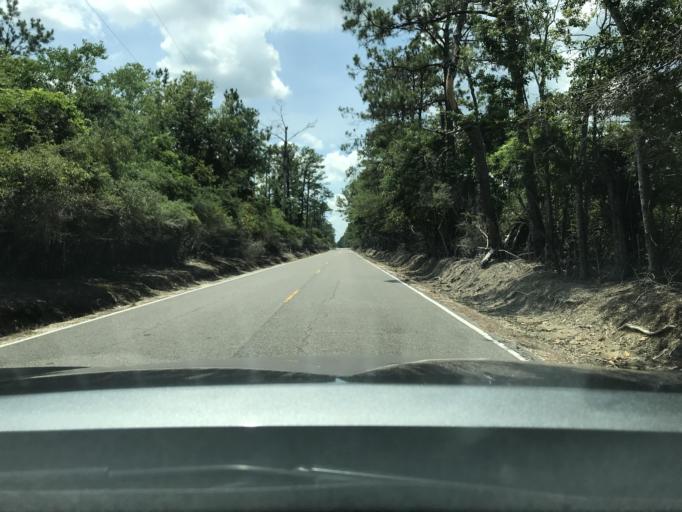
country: US
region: Louisiana
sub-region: Calcasieu Parish
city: Moss Bluff
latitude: 30.3299
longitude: -93.1463
